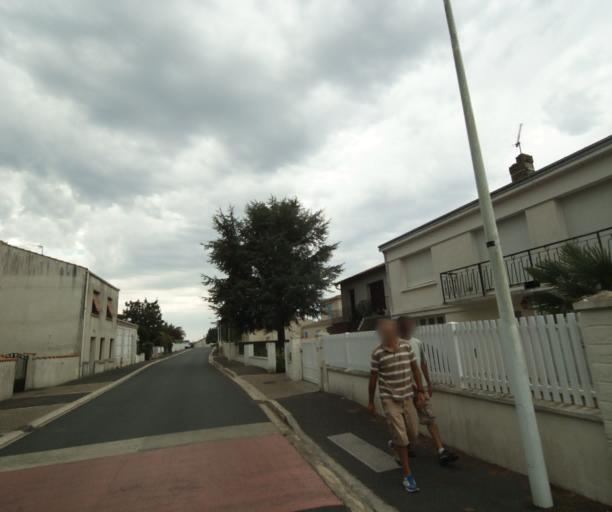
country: FR
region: Poitou-Charentes
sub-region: Departement de la Charente-Maritime
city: Tonnay-Charente
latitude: 45.9479
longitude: -0.8833
